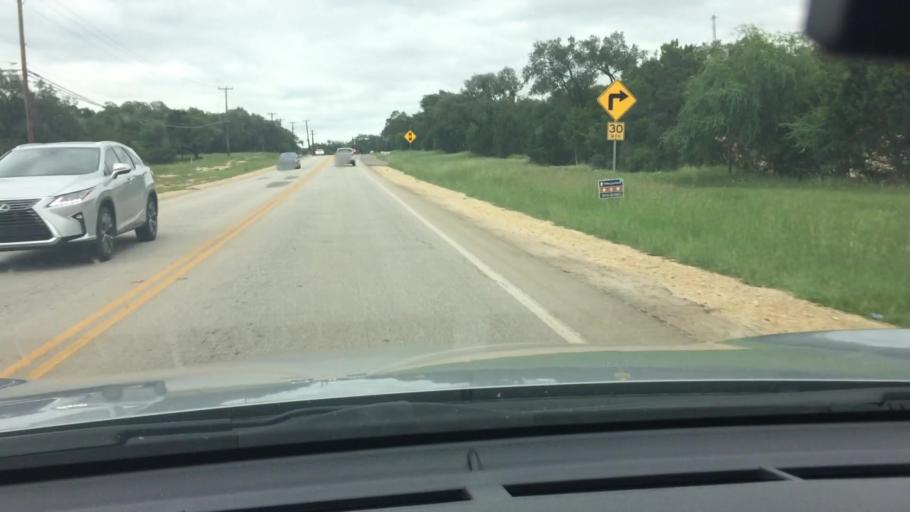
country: US
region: Texas
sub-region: Comal County
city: Garden Ridge
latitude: 29.6413
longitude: -98.3817
